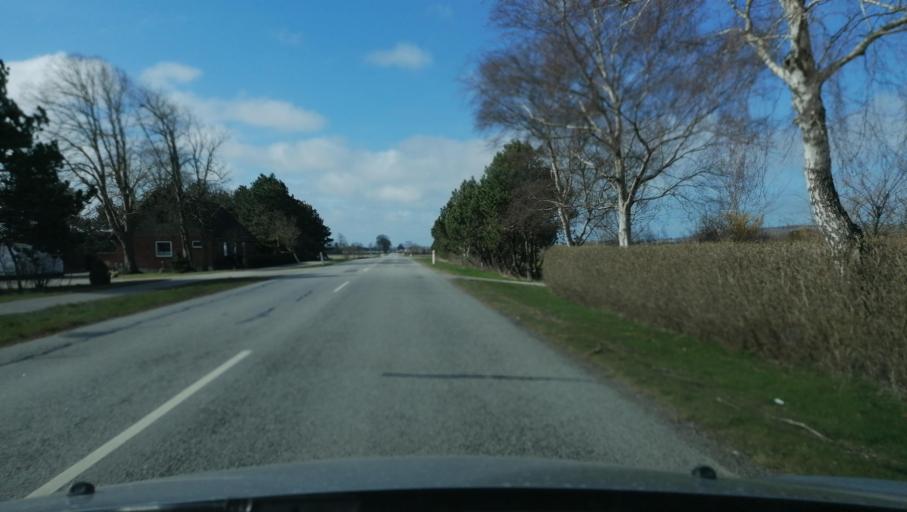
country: DK
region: Zealand
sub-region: Odsherred Kommune
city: Asnaes
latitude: 55.7972
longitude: 11.4679
